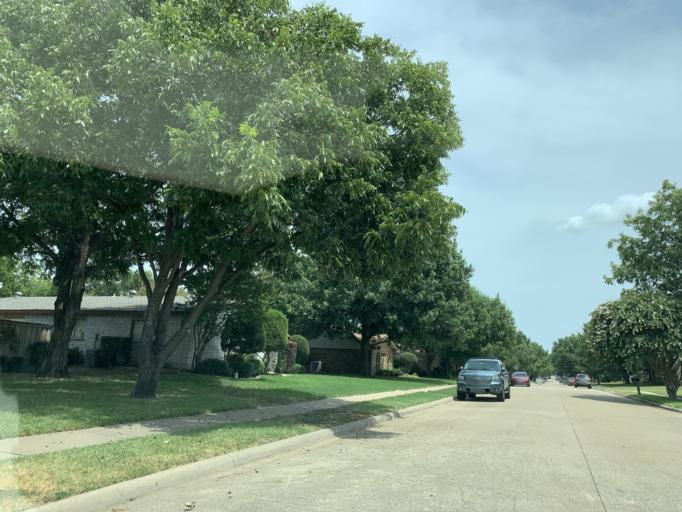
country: US
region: Texas
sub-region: Dallas County
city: Grand Prairie
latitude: 32.6614
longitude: -97.0333
